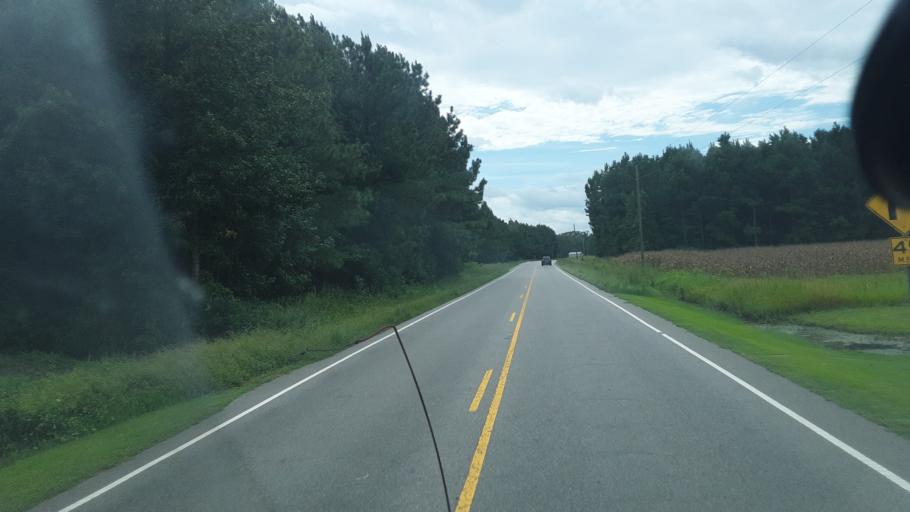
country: US
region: North Carolina
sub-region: Robeson County
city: Rowland
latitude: 34.6266
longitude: -79.3364
